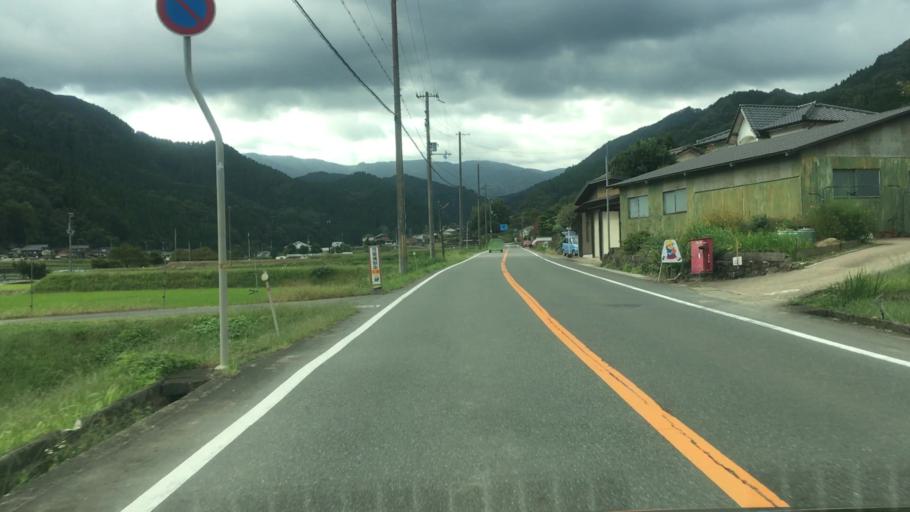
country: JP
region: Hyogo
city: Toyooka
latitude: 35.4110
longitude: 134.7385
